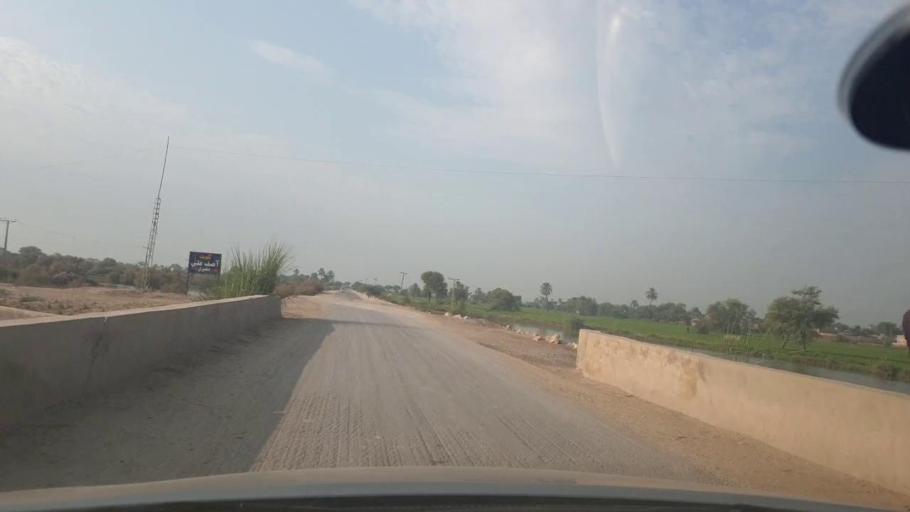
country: PK
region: Sindh
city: Jacobabad
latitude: 28.1979
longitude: 68.3678
